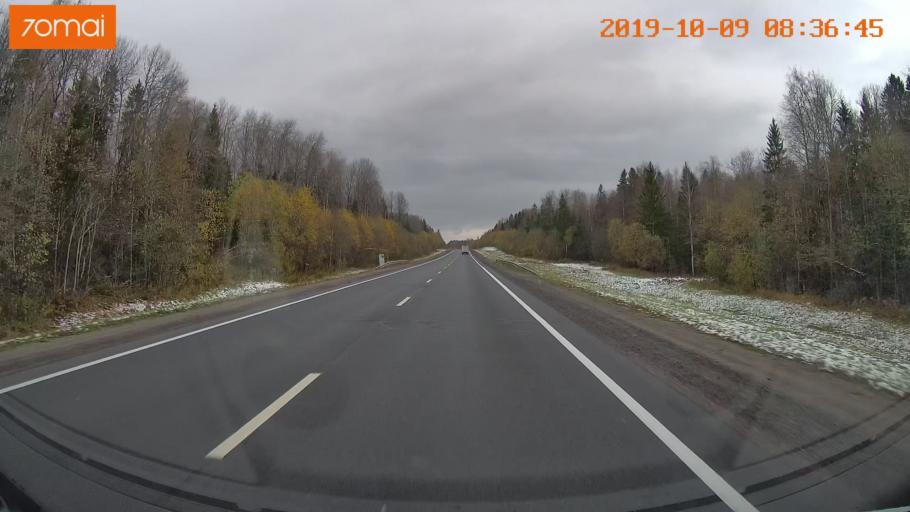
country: RU
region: Vologda
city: Gryazovets
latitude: 58.9310
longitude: 40.1759
